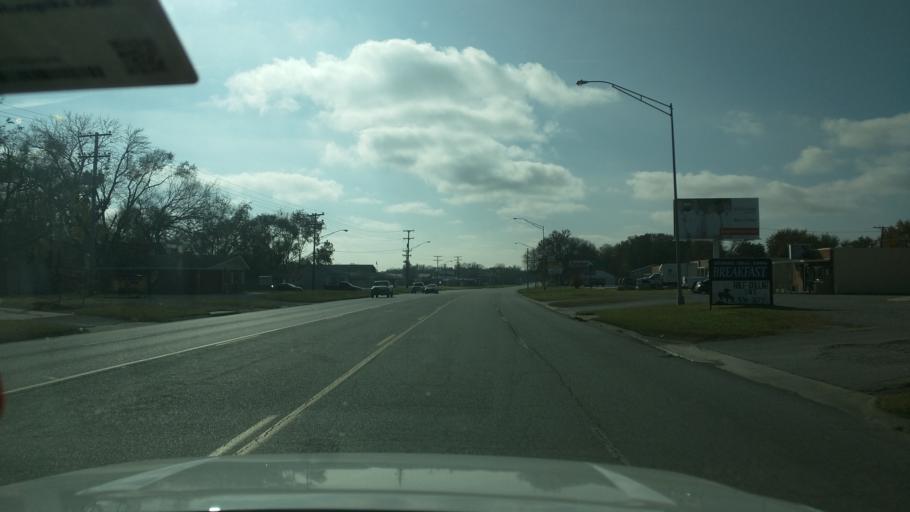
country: US
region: Oklahoma
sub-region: Washington County
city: Dewey
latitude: 36.7915
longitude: -95.9354
